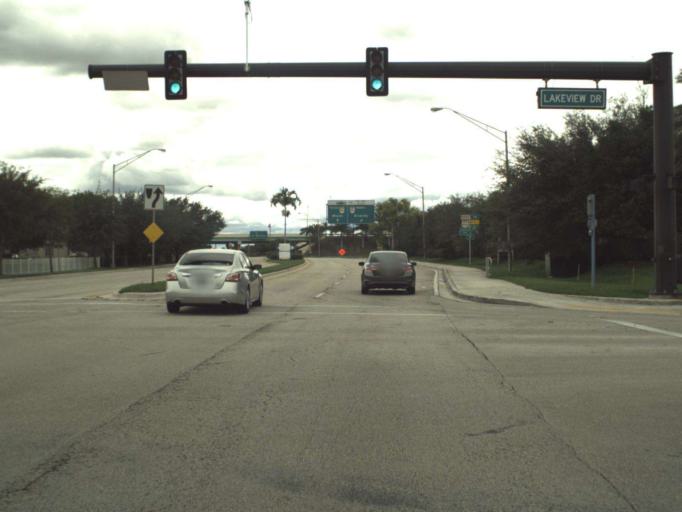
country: US
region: Florida
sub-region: Broward County
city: Coral Springs
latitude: 26.2332
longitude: -80.2928
